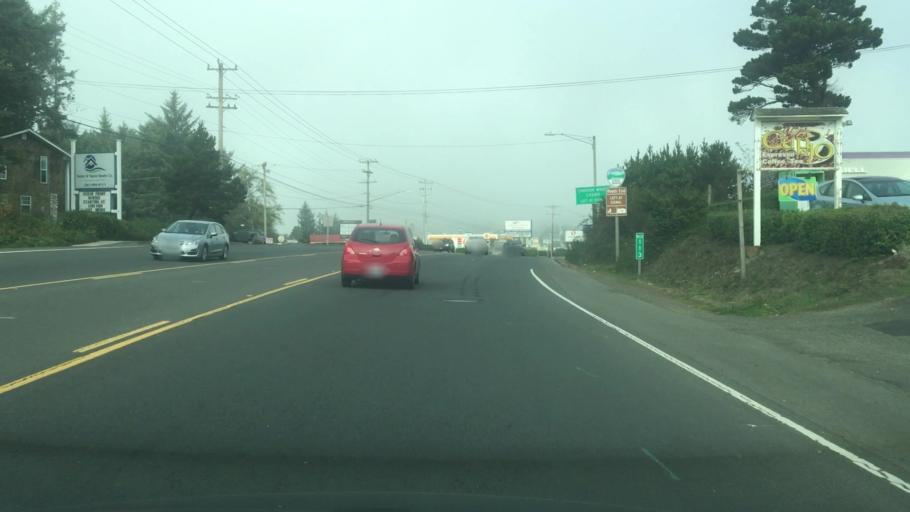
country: US
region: Oregon
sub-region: Lincoln County
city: Lincoln City
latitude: 44.9931
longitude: -124.0064
